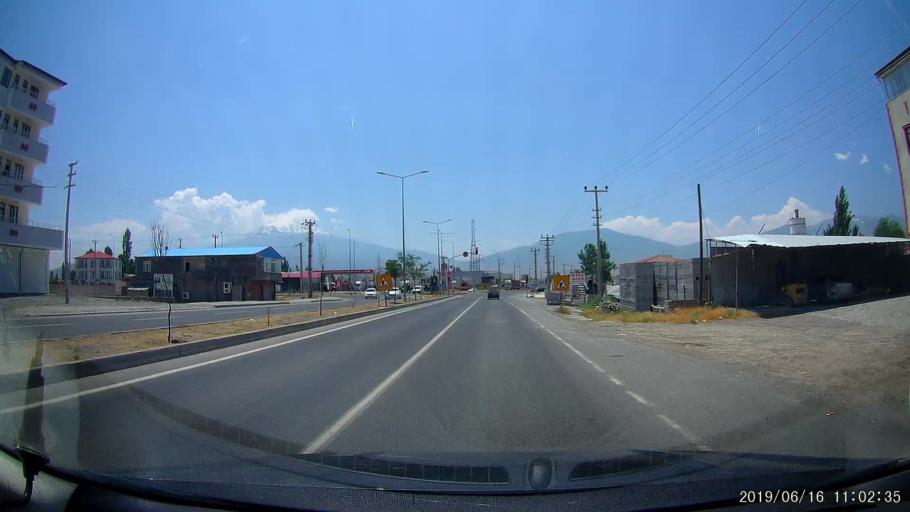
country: TR
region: Igdir
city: Igdir
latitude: 39.9104
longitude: 44.0588
